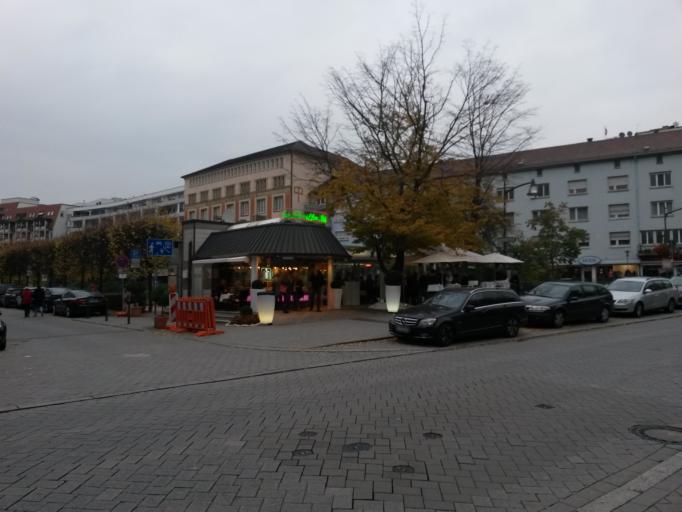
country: DE
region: Baden-Wuerttemberg
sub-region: Karlsruhe Region
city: Pforzheim
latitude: 48.8895
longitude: 8.6982
